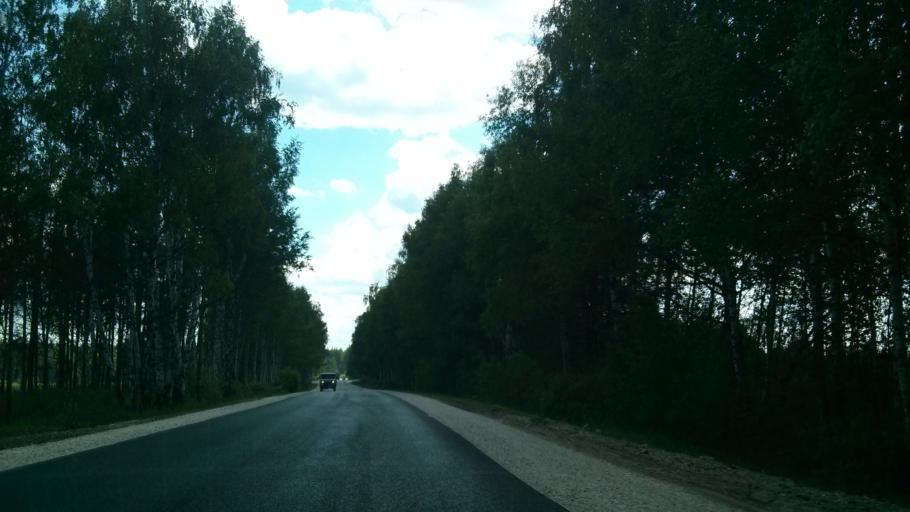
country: RU
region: Vladimir
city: Murom
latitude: 55.5031
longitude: 41.9106
